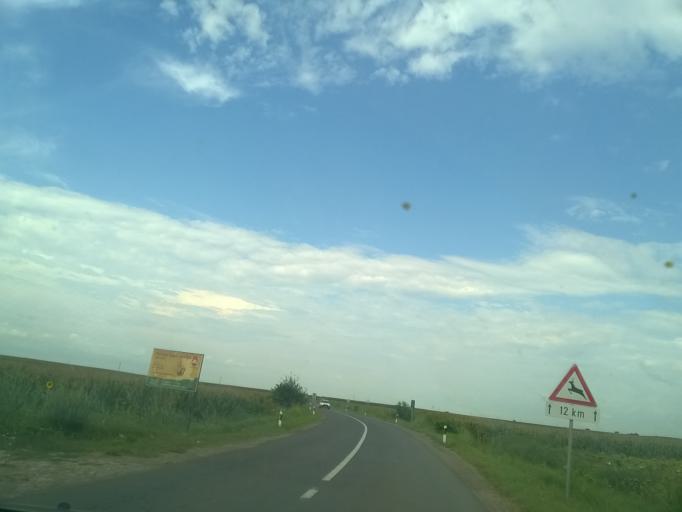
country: RS
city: Orlovat
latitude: 45.2504
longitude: 20.5753
